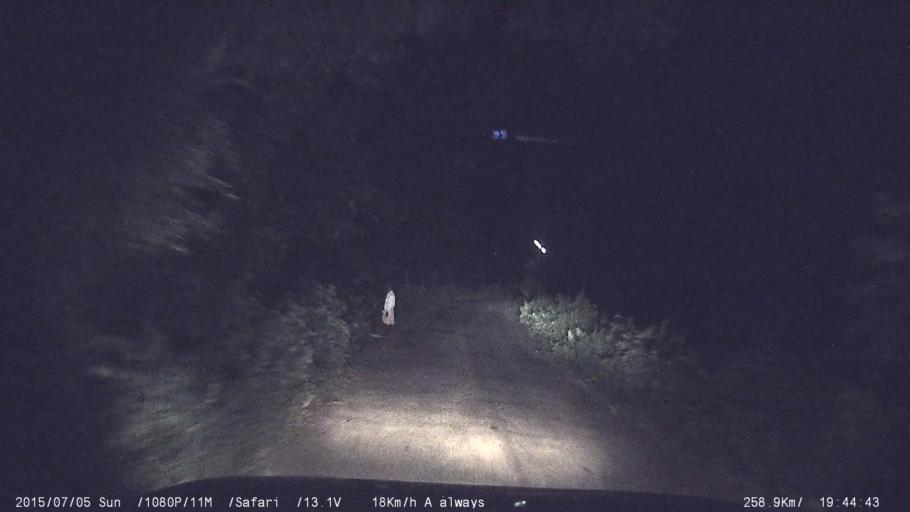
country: IN
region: Kerala
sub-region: Palakkad district
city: Palakkad
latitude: 10.7705
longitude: 76.5512
